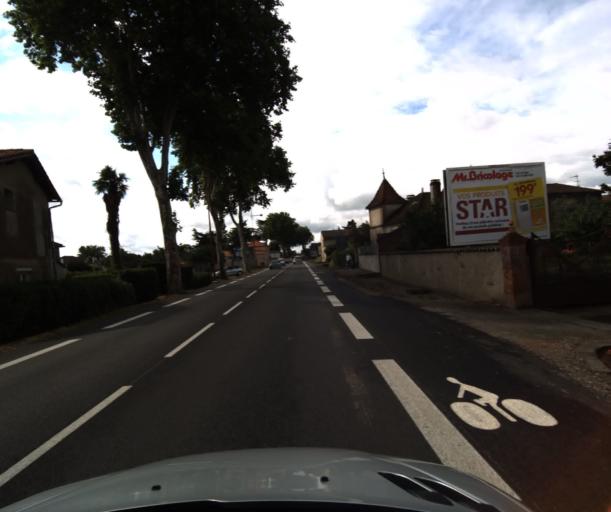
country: FR
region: Midi-Pyrenees
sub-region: Departement du Tarn-et-Garonne
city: Castelsarrasin
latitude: 44.0512
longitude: 1.1016
